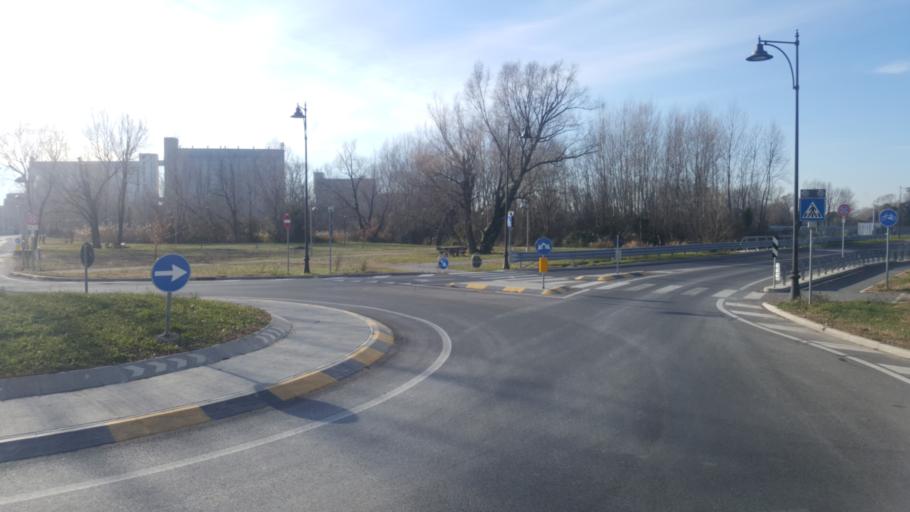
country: IT
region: Friuli Venezia Giulia
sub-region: Provincia di Gorizia
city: Monfalcone
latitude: 45.7912
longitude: 13.5325
